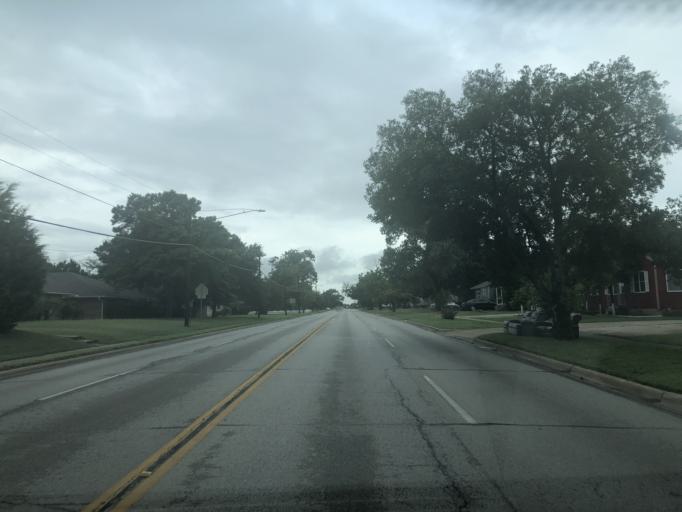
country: US
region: Texas
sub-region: Dallas County
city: Irving
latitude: 32.8012
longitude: -96.9480
